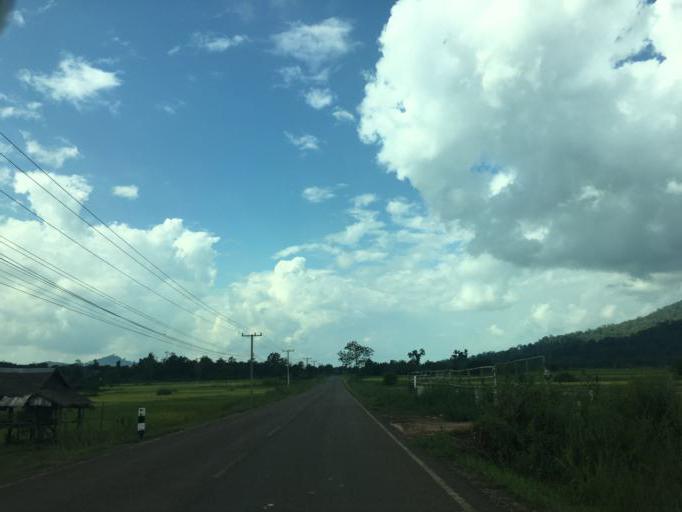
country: TH
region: Nong Khai
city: Sangkhom
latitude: 18.1776
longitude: 102.2513
